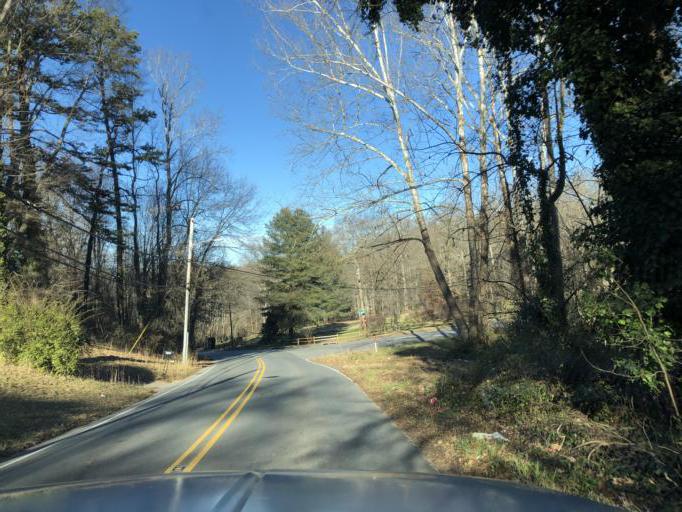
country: US
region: North Carolina
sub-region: Cleveland County
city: Shelby
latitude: 35.3062
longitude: -81.5387
